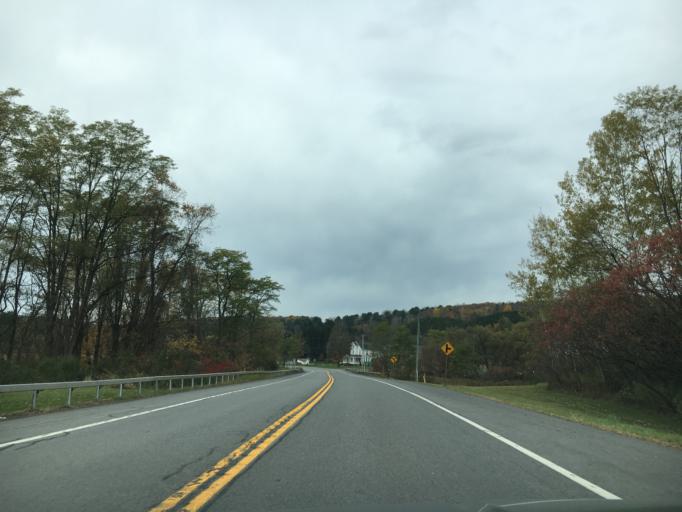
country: US
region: New York
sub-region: Otsego County
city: Oneonta
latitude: 42.5300
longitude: -74.9774
